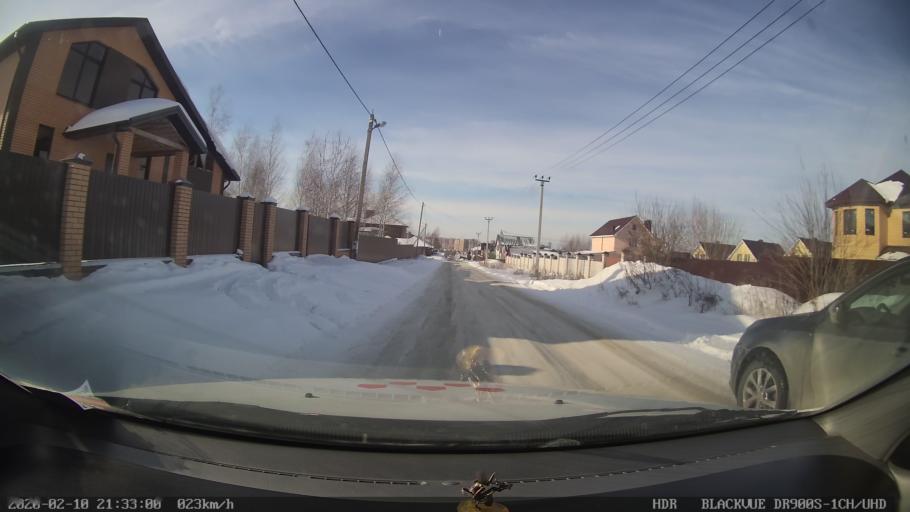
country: RU
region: Tatarstan
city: Vysokaya Gora
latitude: 55.7796
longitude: 49.2734
